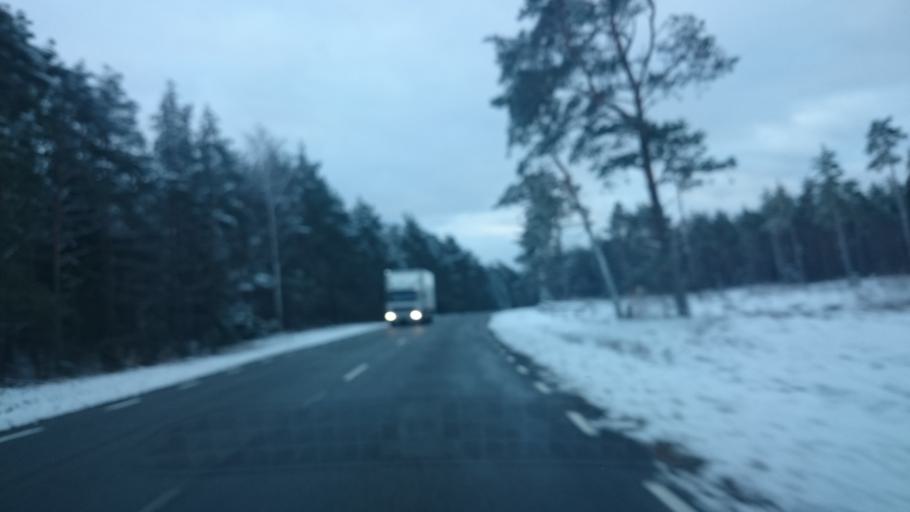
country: EE
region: Saare
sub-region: Kuressaare linn
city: Kuressaare
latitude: 58.3943
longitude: 22.6469
